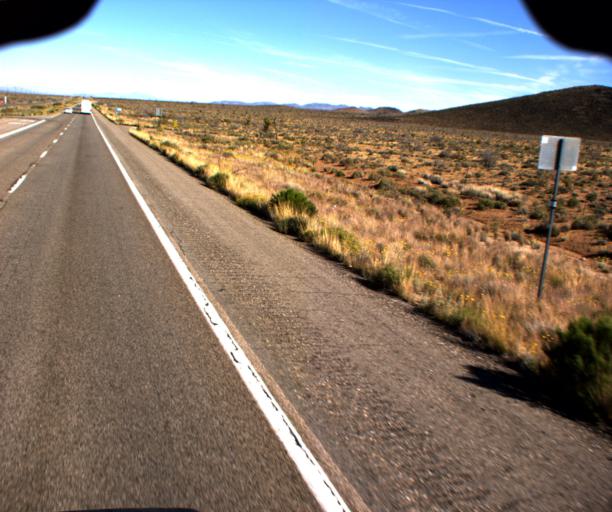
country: US
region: Arizona
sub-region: Mohave County
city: Dolan Springs
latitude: 35.4552
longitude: -114.3008
